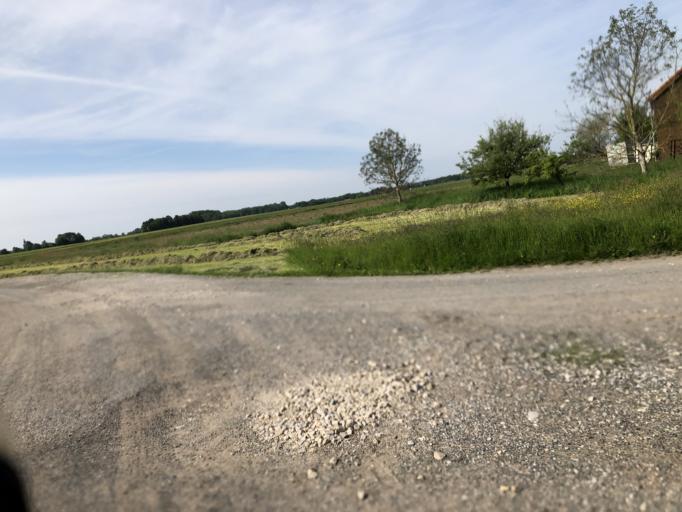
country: DE
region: Bavaria
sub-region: Regierungsbezirk Mittelfranken
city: Erlangen
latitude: 49.5445
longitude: 11.0105
